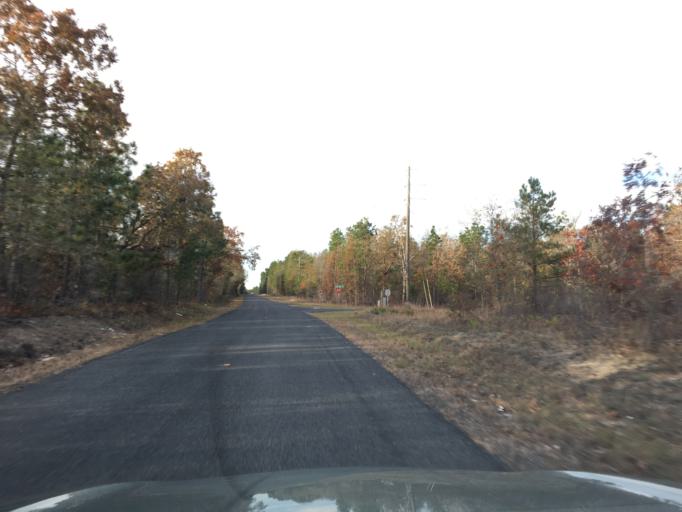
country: US
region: South Carolina
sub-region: Lexington County
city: Leesville
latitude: 33.6837
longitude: -81.3781
